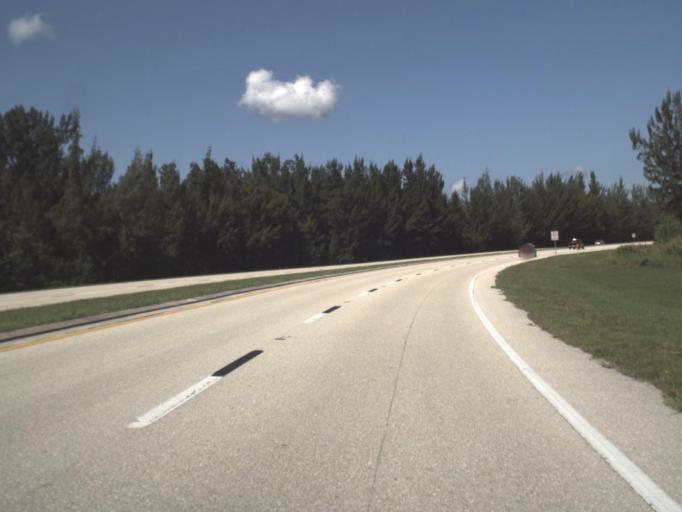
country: US
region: Florida
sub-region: Lee County
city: Pine Island Center
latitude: 26.6083
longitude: -82.0343
